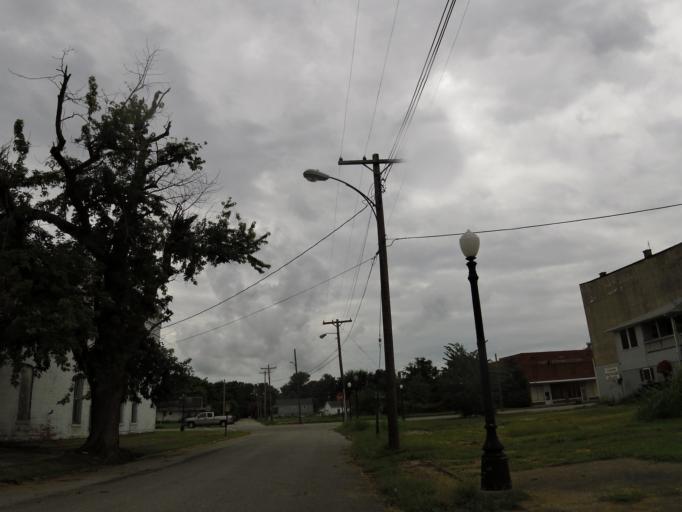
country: US
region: Illinois
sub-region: Alexander County
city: Cairo
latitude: 36.9998
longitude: -89.1664
